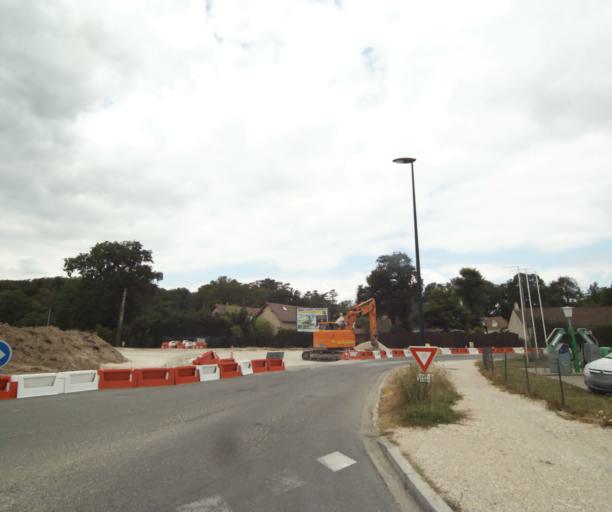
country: FR
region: Centre
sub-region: Departement du Loiret
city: Checy
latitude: 47.9049
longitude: 2.0308
